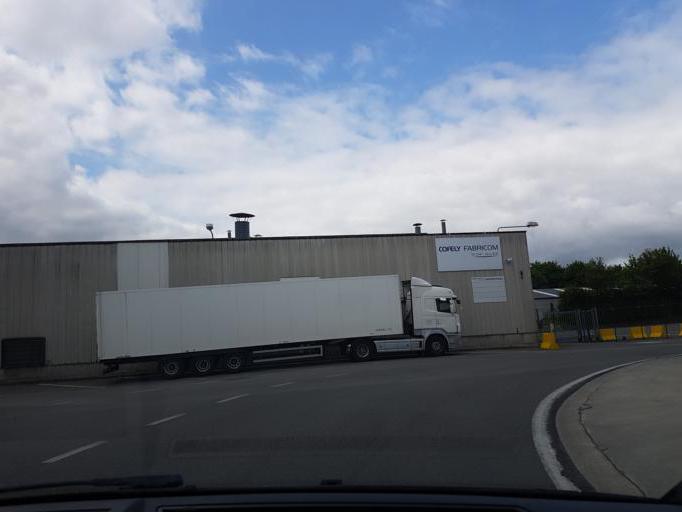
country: BE
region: Flanders
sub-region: Provincie Vlaams-Brabant
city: Vilvoorde
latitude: 50.9437
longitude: 4.4104
